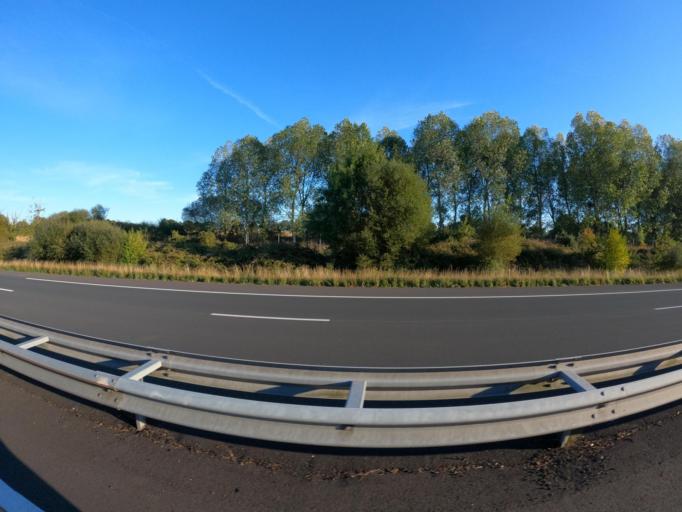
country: FR
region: Pays de la Loire
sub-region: Departement de la Vendee
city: Vendrennes
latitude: 46.8691
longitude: -1.1261
